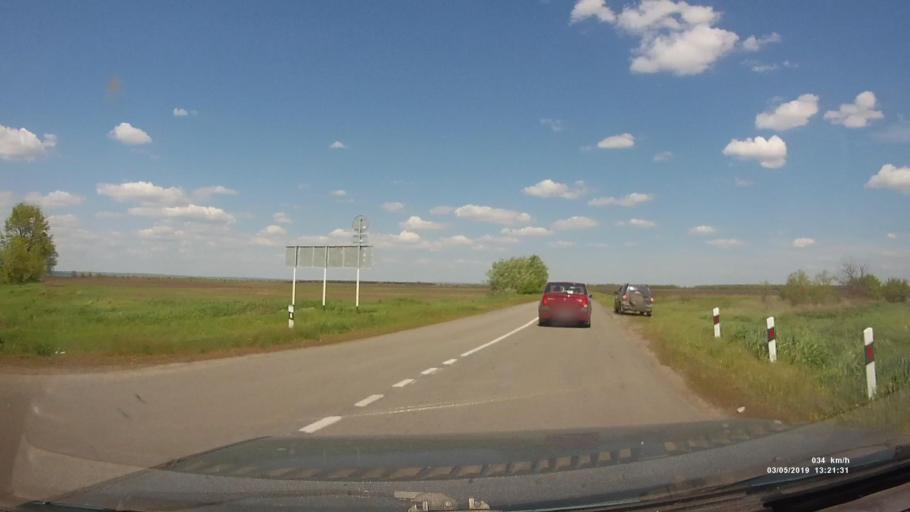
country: RU
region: Rostov
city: Semikarakorsk
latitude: 47.5553
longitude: 40.7471
